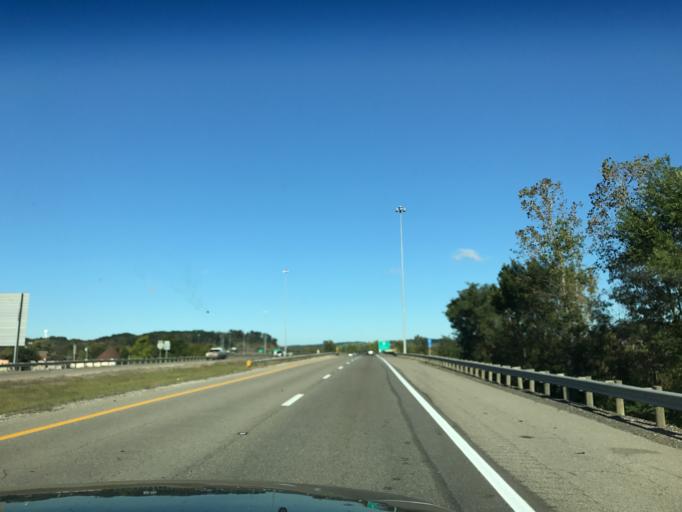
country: US
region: West Virginia
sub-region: Wood County
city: Parkersburg
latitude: 39.2552
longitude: -81.5450
